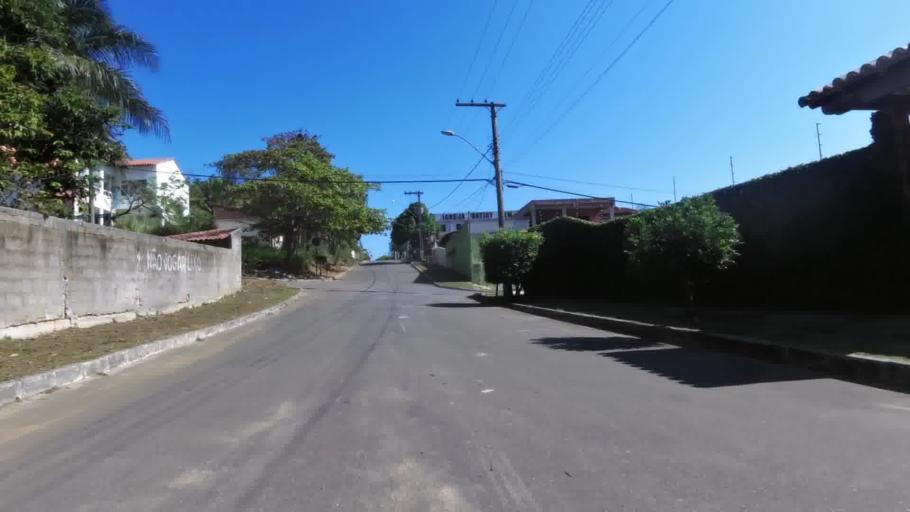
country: BR
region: Espirito Santo
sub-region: Guarapari
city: Guarapari
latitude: -20.7355
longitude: -40.5434
